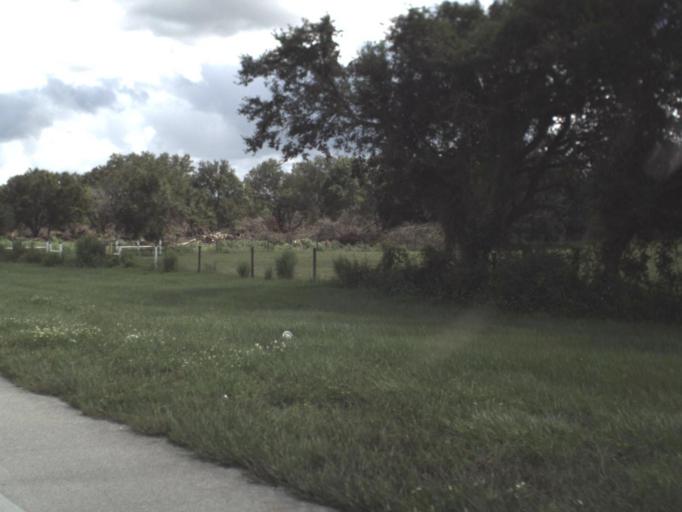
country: US
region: Florida
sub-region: DeSoto County
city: Southeast Arcadia
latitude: 27.2087
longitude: -81.7716
